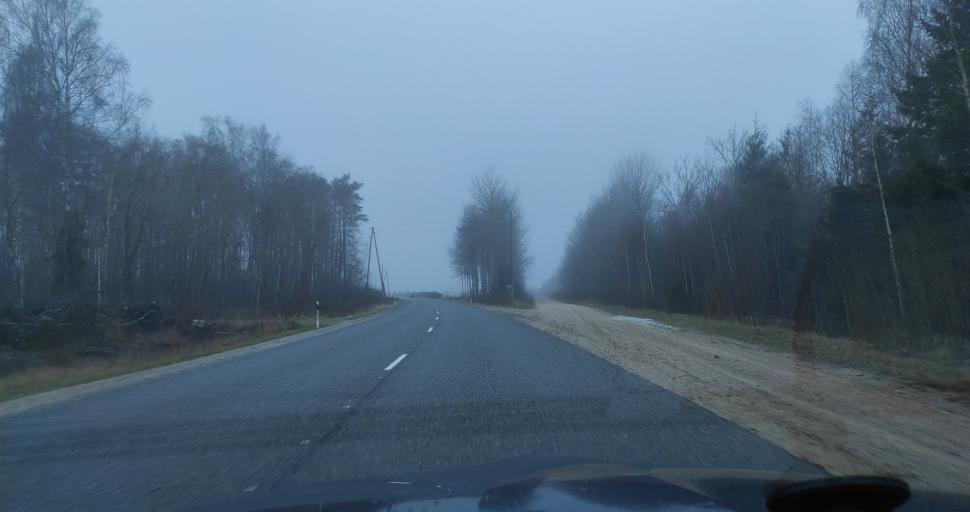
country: LV
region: Alsunga
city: Alsunga
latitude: 56.9942
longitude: 21.3698
